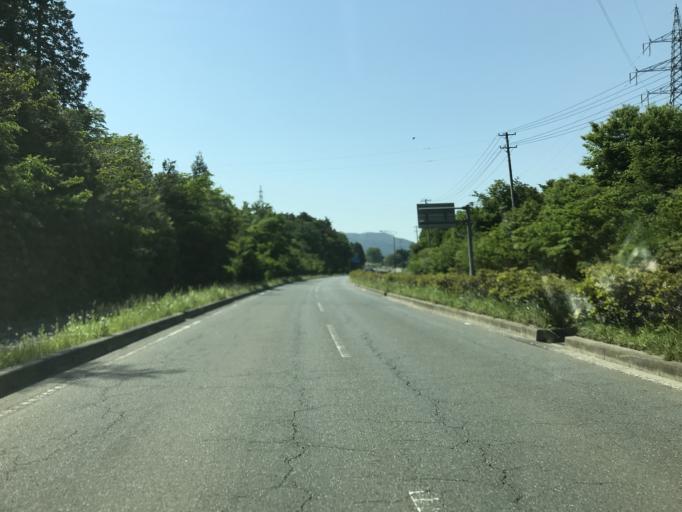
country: JP
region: Miyagi
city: Marumori
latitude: 37.8378
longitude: 140.9154
